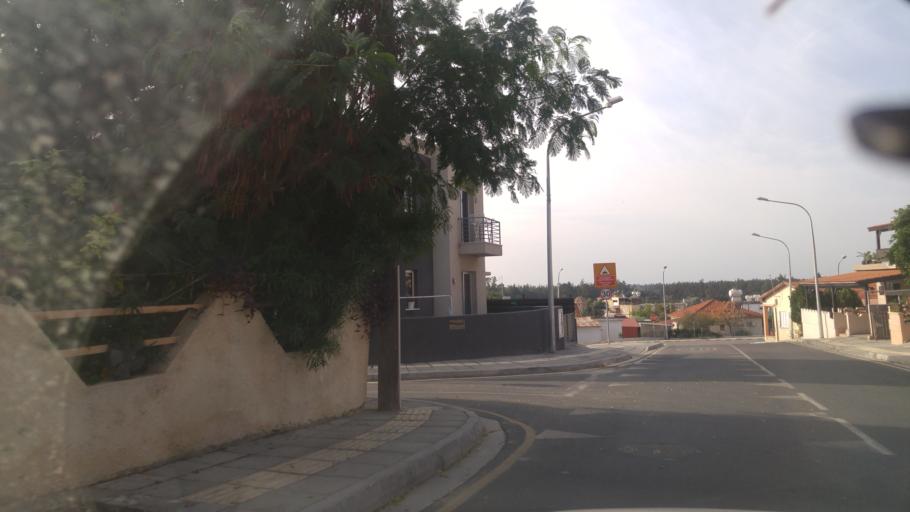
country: CY
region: Limassol
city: Ypsonas
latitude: 34.6562
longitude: 32.9683
